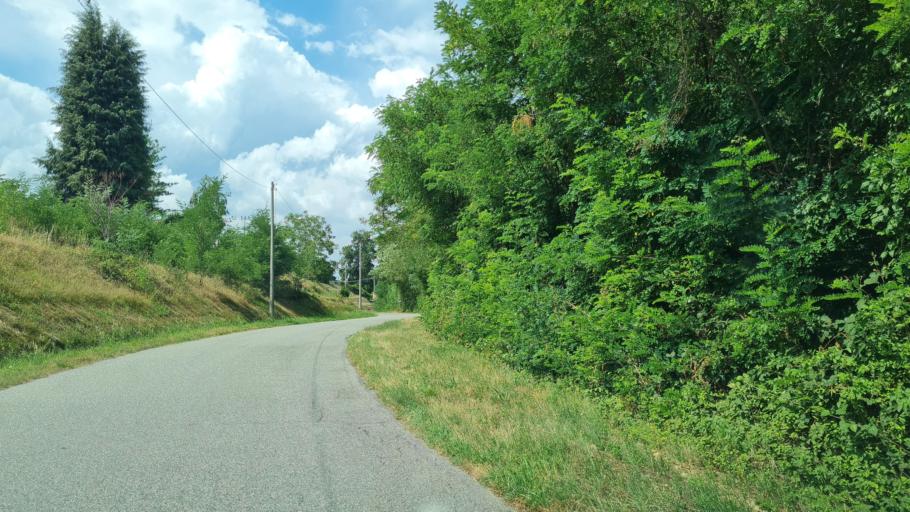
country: IT
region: Piedmont
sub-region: Provincia di Biella
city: Lessona
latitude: 45.5791
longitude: 8.2108
